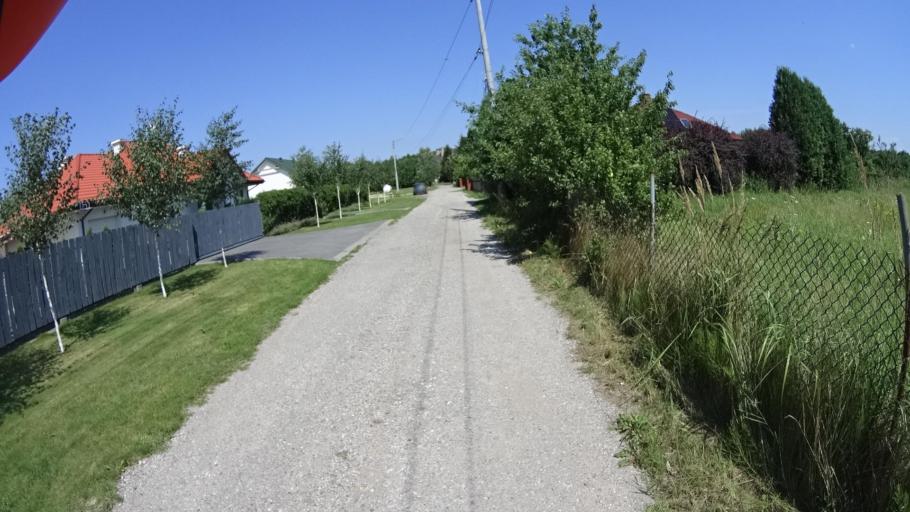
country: PL
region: Masovian Voivodeship
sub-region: Powiat piaseczynski
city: Tarczyn
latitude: 51.9796
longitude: 20.8733
